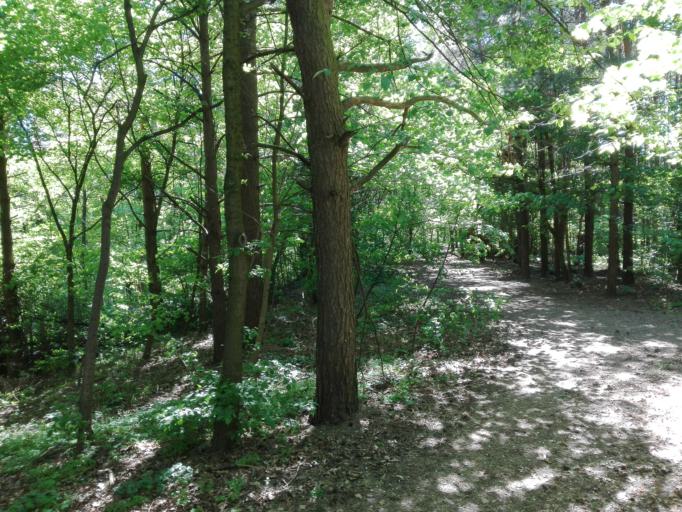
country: LT
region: Vilnius County
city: Lazdynai
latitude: 54.6860
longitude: 25.2165
